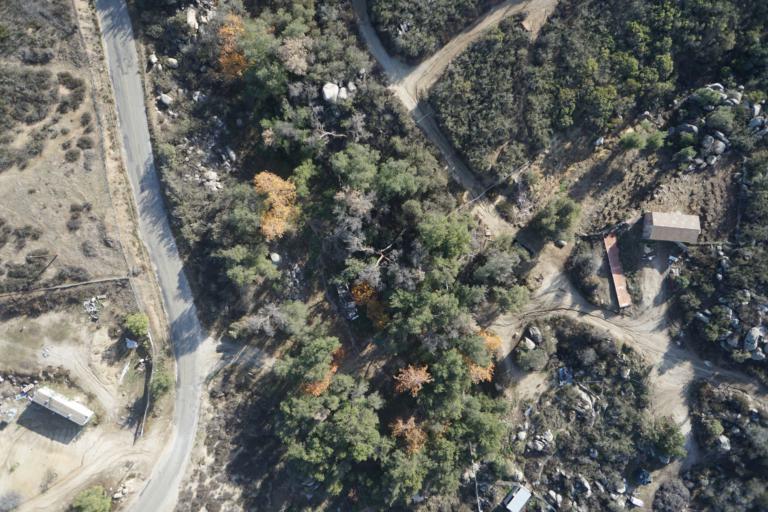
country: US
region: California
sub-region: Riverside County
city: East Hemet
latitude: 33.6404
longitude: -116.9226
